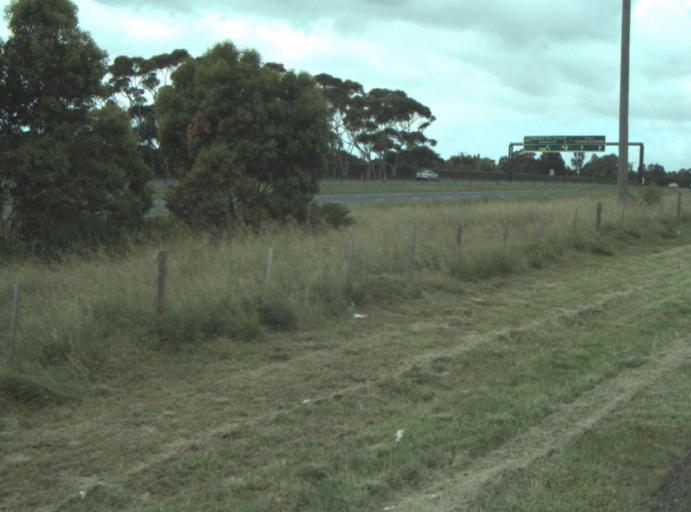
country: AU
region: Victoria
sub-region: Greater Geelong
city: Lara
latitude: -38.0445
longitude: 144.4056
